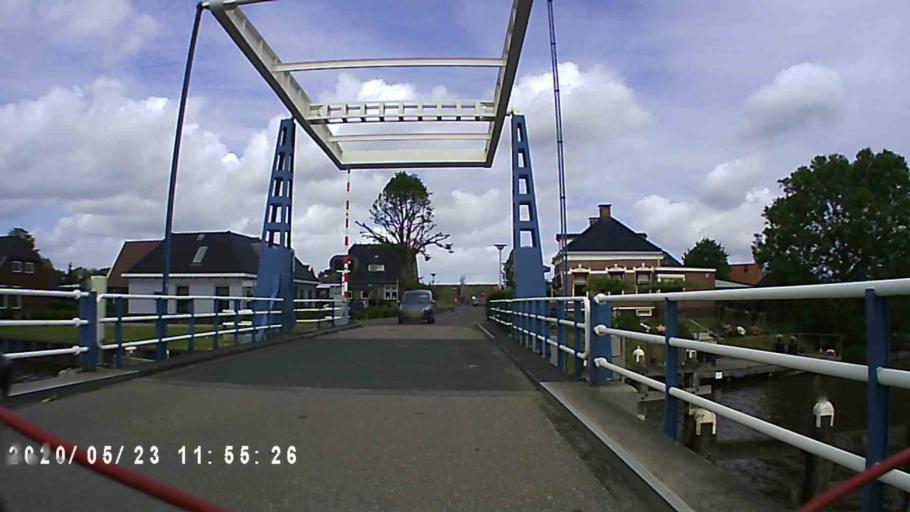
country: NL
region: Groningen
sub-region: Gemeente Delfzijl
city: Delfzijl
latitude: 53.3006
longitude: 7.0354
